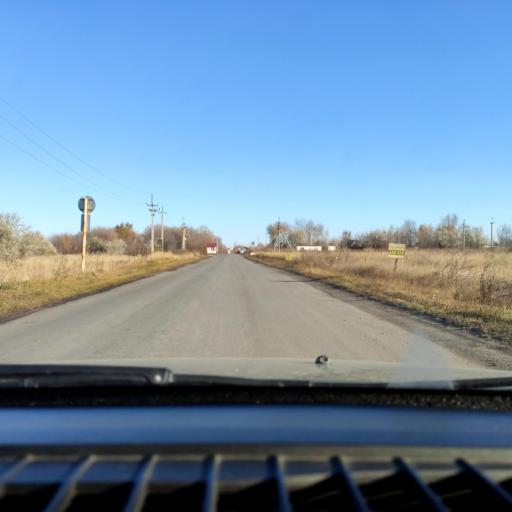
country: RU
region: Samara
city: Tol'yatti
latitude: 53.6580
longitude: 49.3318
